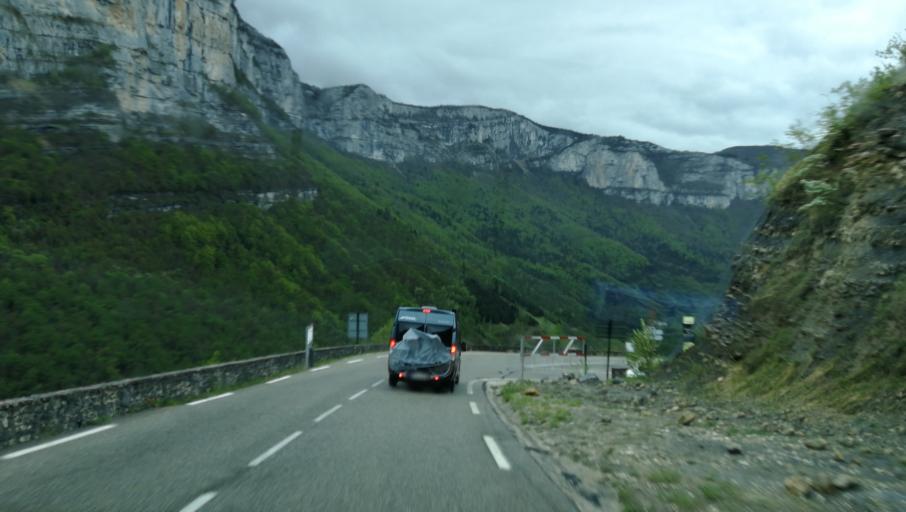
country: FR
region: Rhone-Alpes
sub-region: Departement de l'Isere
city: Pont-en-Royans
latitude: 45.0642
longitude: 5.4269
